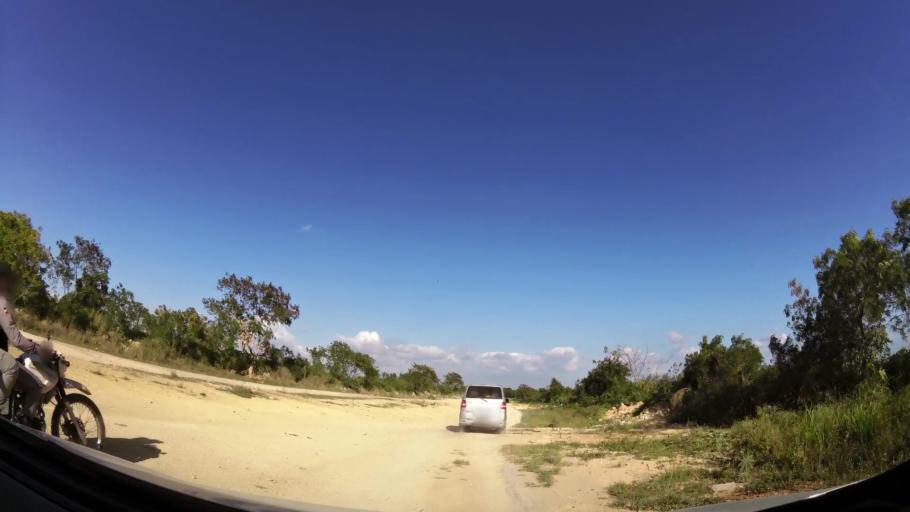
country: DO
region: Santo Domingo
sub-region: Santo Domingo
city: Santo Domingo Este
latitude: 18.4831
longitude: -69.8002
